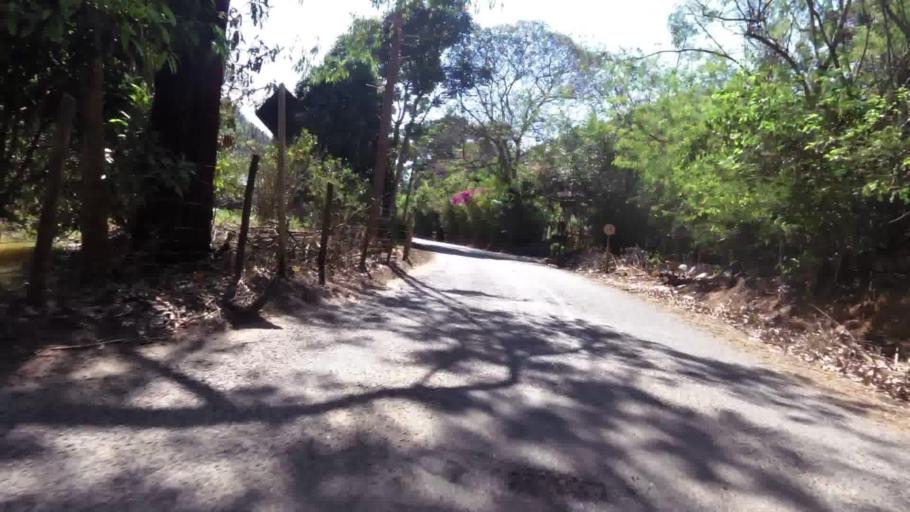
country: BR
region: Espirito Santo
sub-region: Marechal Floriano
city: Marechal Floriano
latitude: -20.4470
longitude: -40.8872
